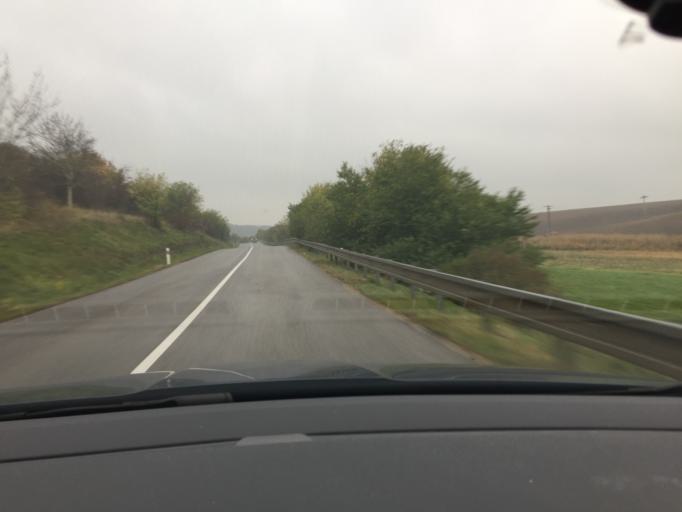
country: SK
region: Nitriansky
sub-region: Okres Nove Zamky
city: Sturovo
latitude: 47.8529
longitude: 18.7304
